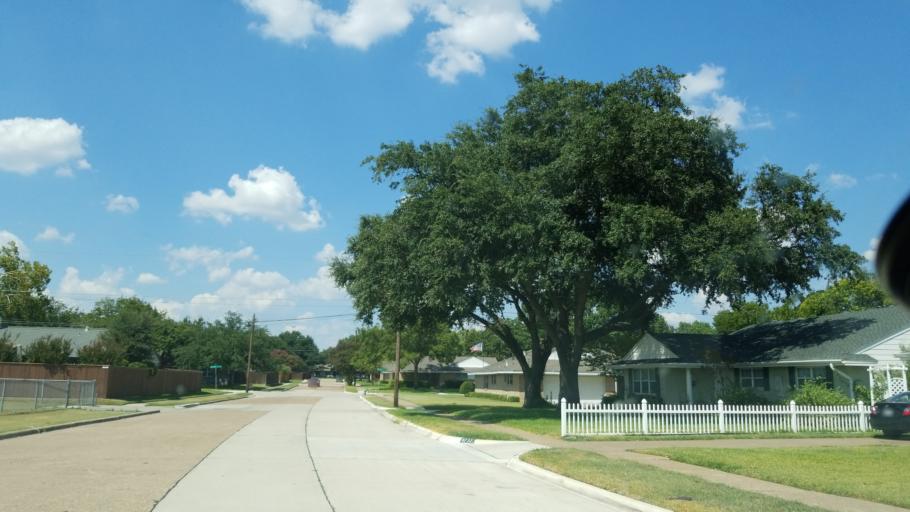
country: US
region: Texas
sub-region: Dallas County
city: Richardson
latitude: 32.8803
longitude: -96.7047
